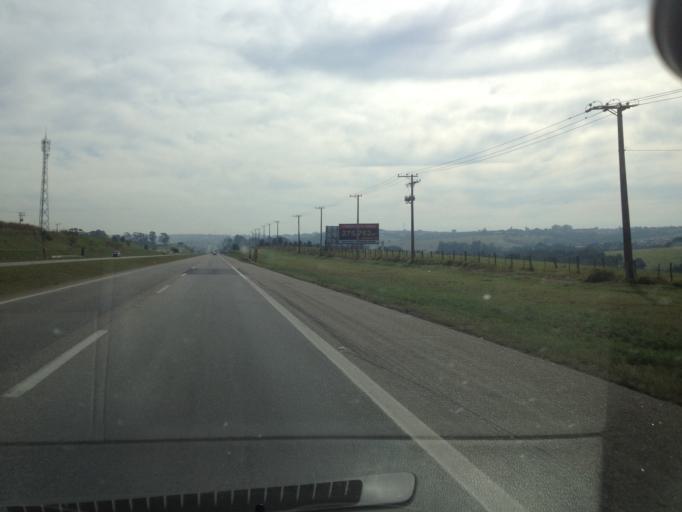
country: BR
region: Sao Paulo
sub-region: Itu
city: Itu
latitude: -23.2890
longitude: -47.3297
